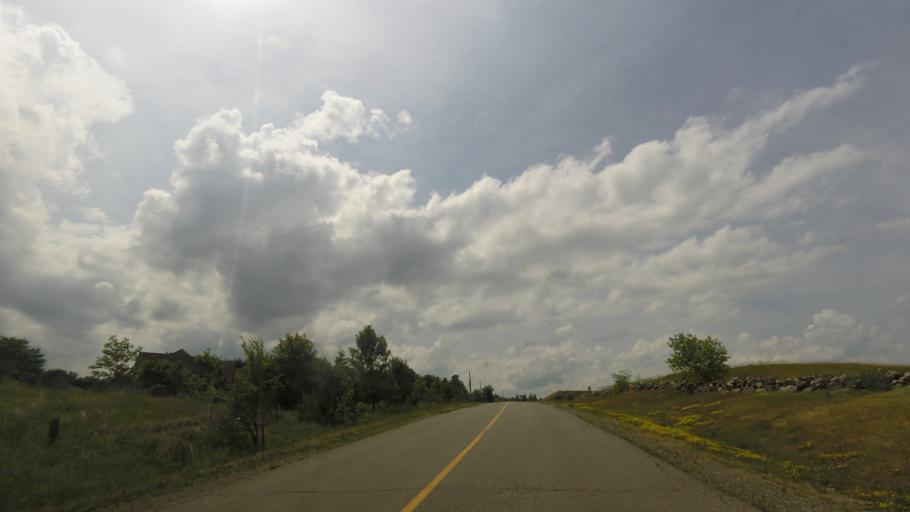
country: CA
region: Ontario
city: Orangeville
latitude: 43.8750
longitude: -79.9165
